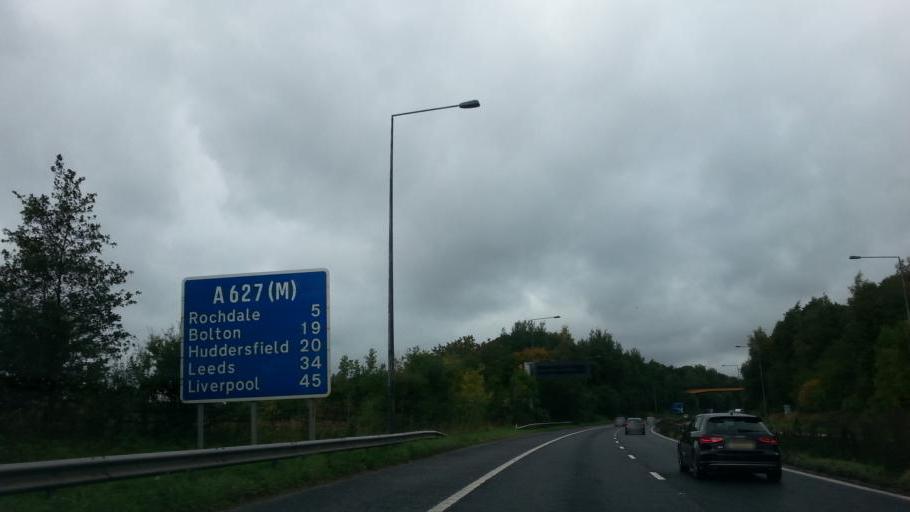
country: GB
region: England
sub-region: Borough of Oldham
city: Royton
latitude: 53.5613
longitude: -2.1493
